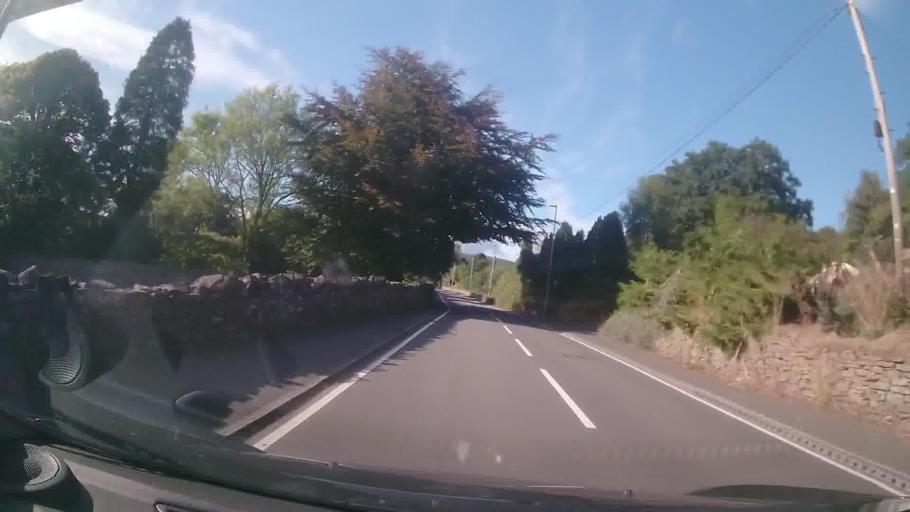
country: GB
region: Wales
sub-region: Blaenau Gwent
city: Brynmawr
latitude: 51.8853
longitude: -3.1839
